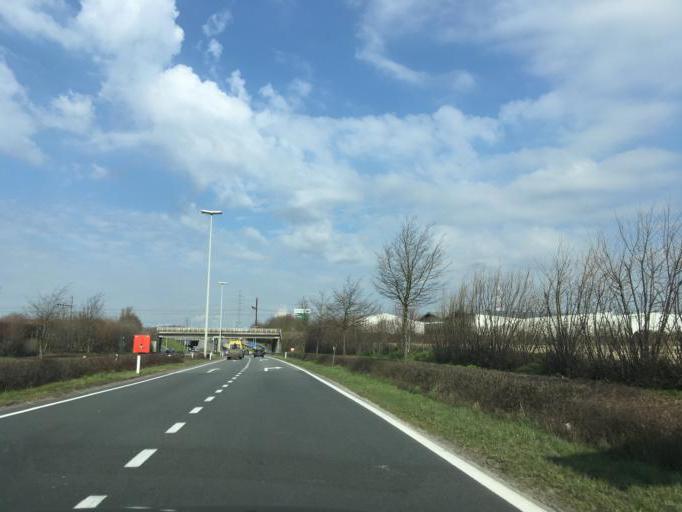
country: BE
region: Flanders
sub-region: Provincie West-Vlaanderen
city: Harelbeke
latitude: 50.8604
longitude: 3.3291
